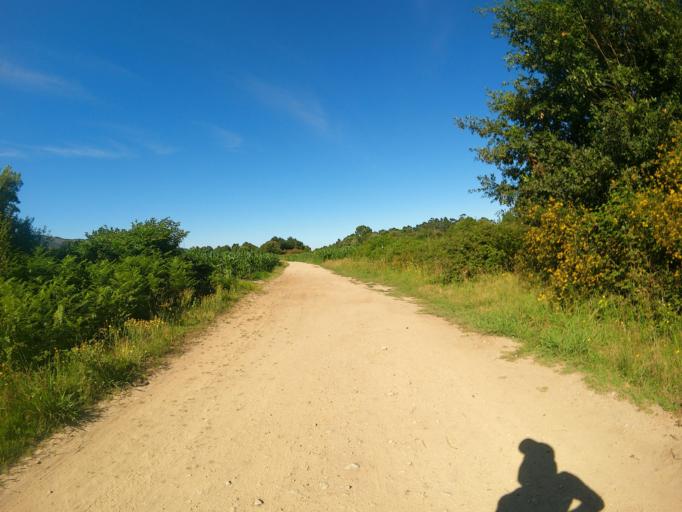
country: PT
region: Viana do Castelo
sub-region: Ponte de Lima
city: Ponte de Lima
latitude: 41.7422
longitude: -8.6413
